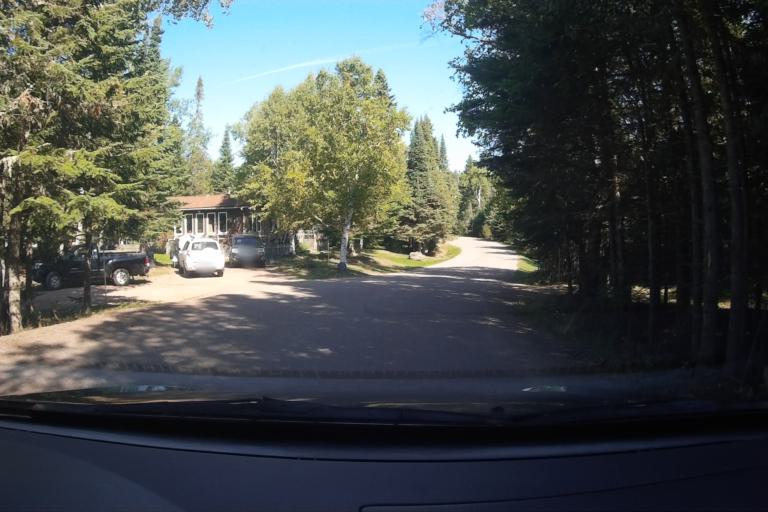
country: CA
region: Ontario
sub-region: Thunder Bay District
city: Thunder Bay
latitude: 48.3344
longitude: -88.8239
